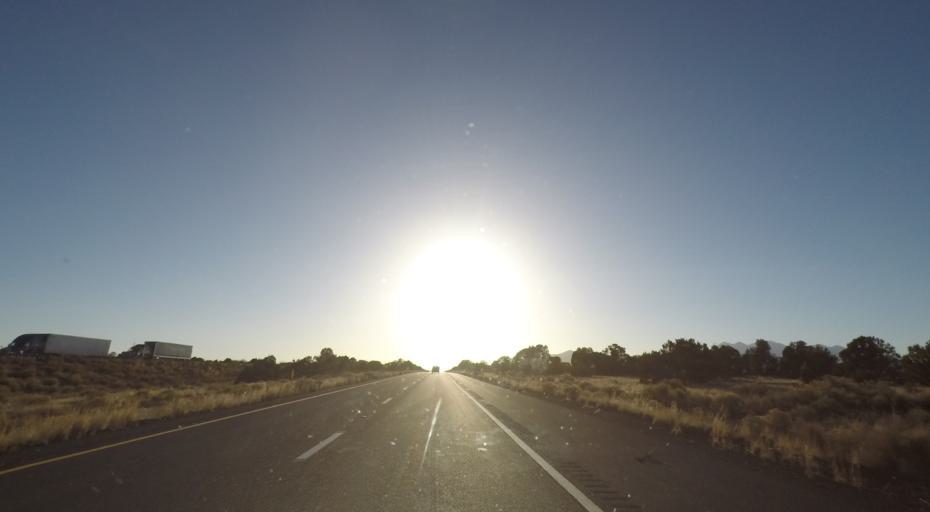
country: US
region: Arizona
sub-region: Coconino County
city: Flagstaff
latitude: 35.2021
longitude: -111.4387
